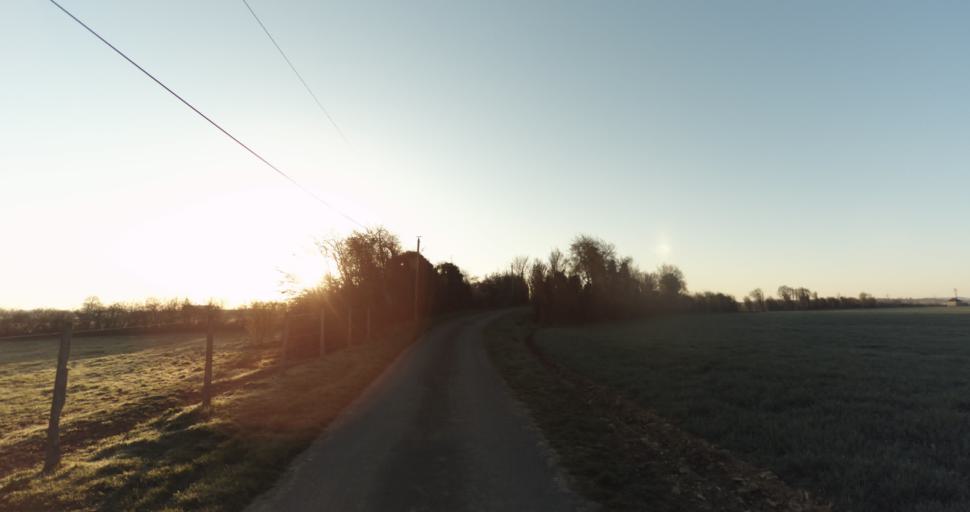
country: FR
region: Lower Normandy
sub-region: Departement du Calvados
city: Saint-Pierre-sur-Dives
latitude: 49.0376
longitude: -0.0370
